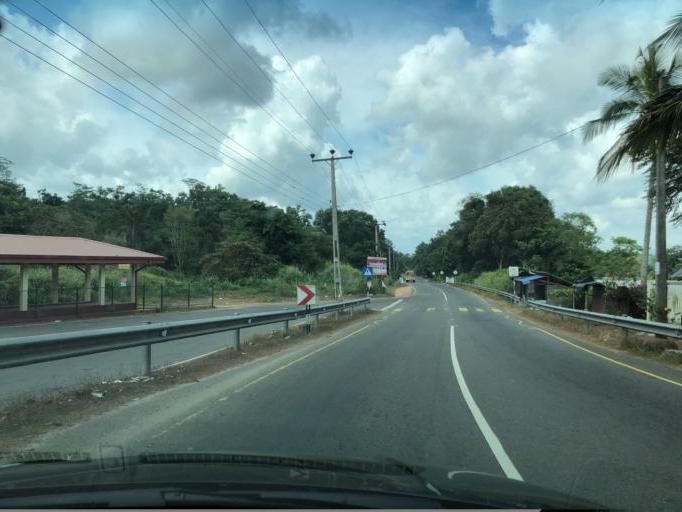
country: LK
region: Western
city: Horana South
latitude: 6.6253
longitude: 80.0734
